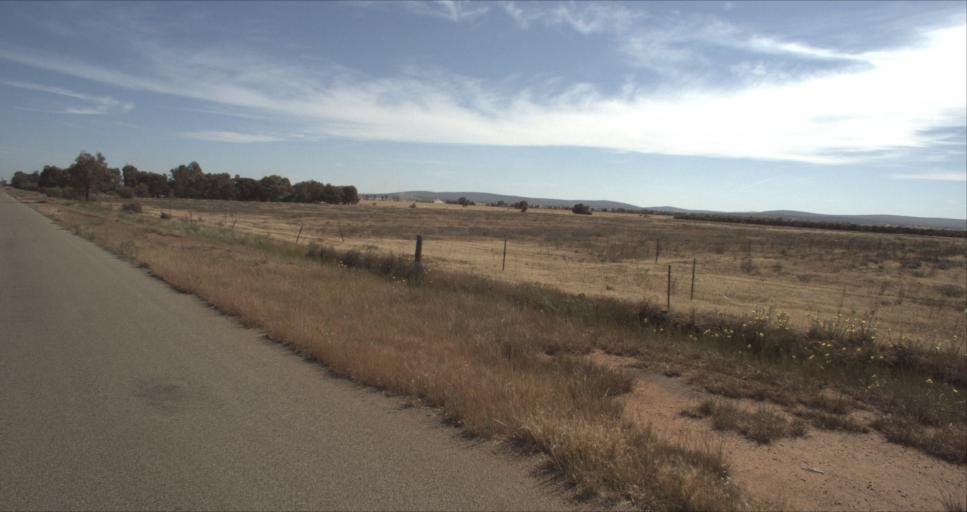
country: AU
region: New South Wales
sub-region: Leeton
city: Leeton
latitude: -34.5769
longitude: 146.4775
